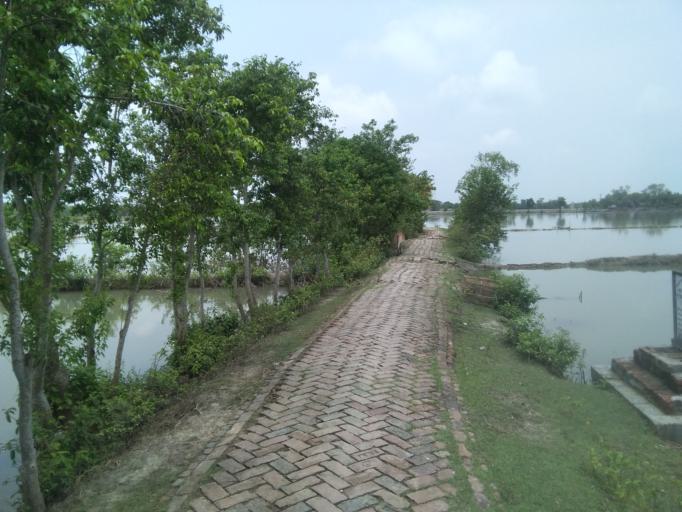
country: BD
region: Khulna
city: Phultala
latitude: 22.6395
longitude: 89.4043
